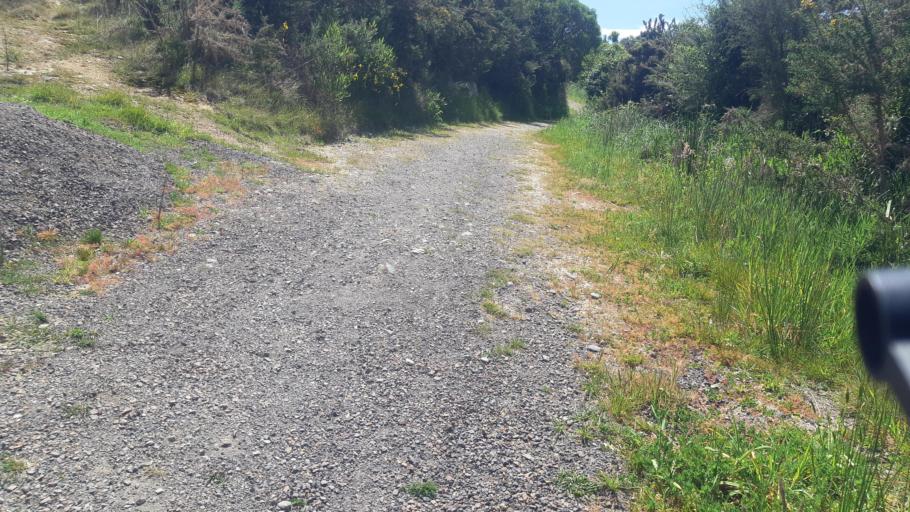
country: NZ
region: Marlborough
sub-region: Marlborough District
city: Picton
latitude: -41.2709
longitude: 174.0242
